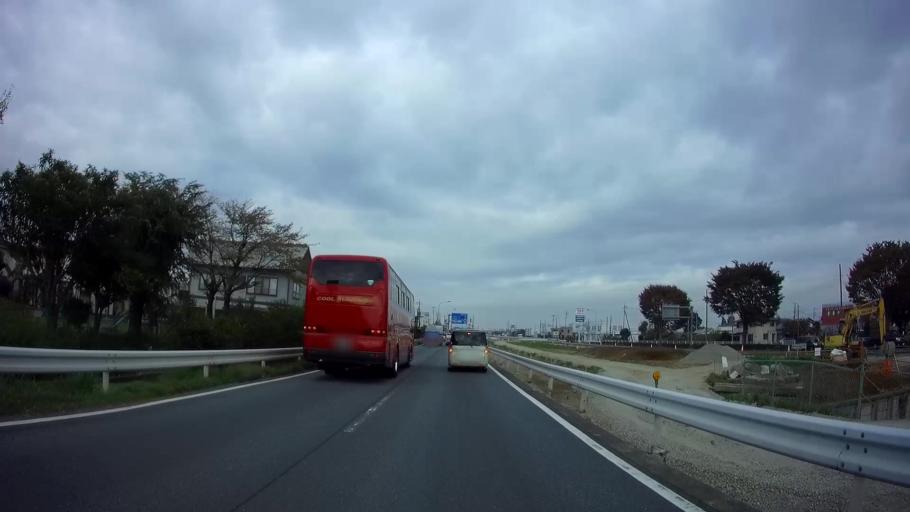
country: JP
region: Saitama
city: Kumagaya
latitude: 36.1603
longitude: 139.4027
